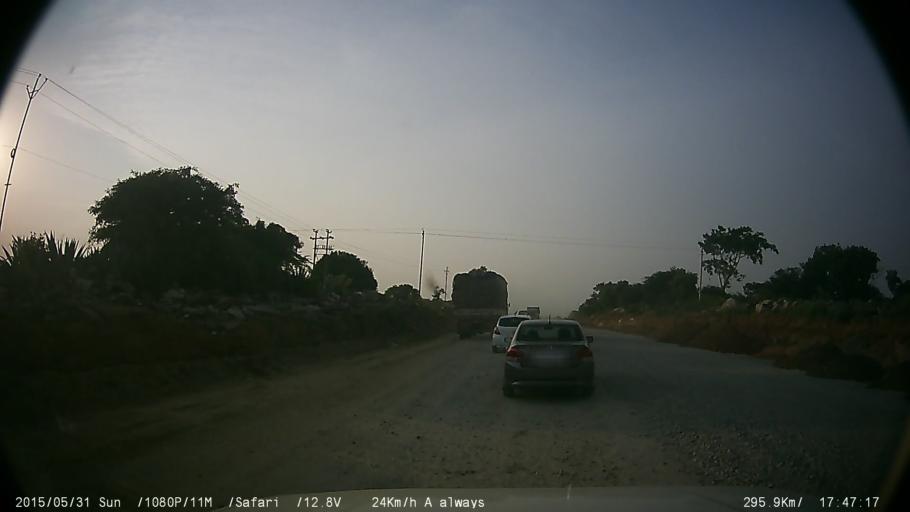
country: IN
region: Karnataka
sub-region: Chamrajnagar
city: Gundlupet
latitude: 11.9616
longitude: 76.6704
